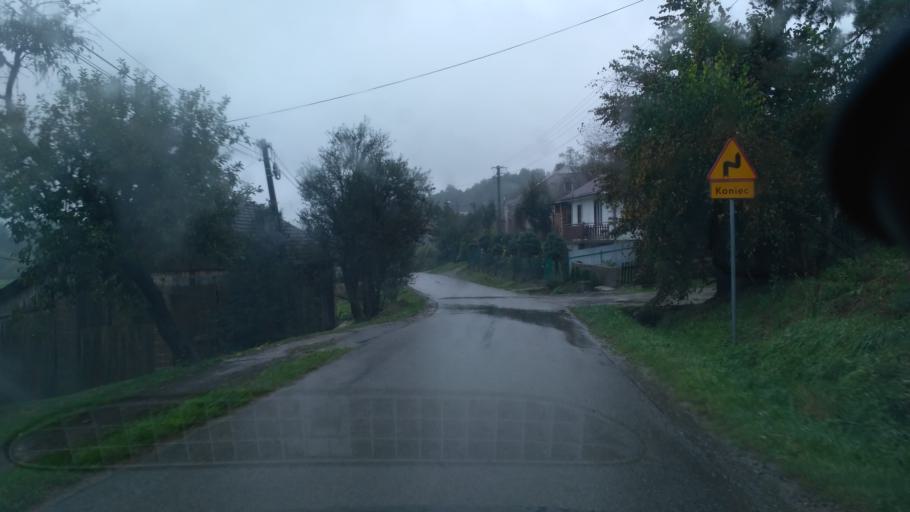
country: PL
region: Subcarpathian Voivodeship
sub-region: Powiat ropczycko-sedziszowski
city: Niedzwiada
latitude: 50.0147
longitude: 21.5469
